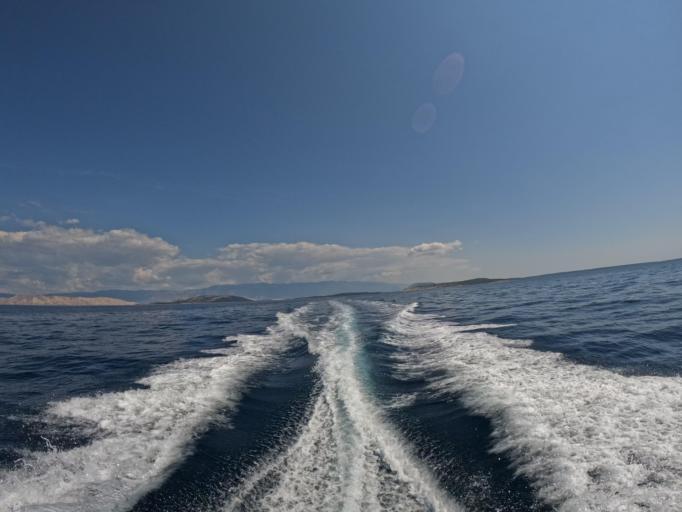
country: HR
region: Primorsko-Goranska
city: Lopar
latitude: 44.8782
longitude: 14.6559
